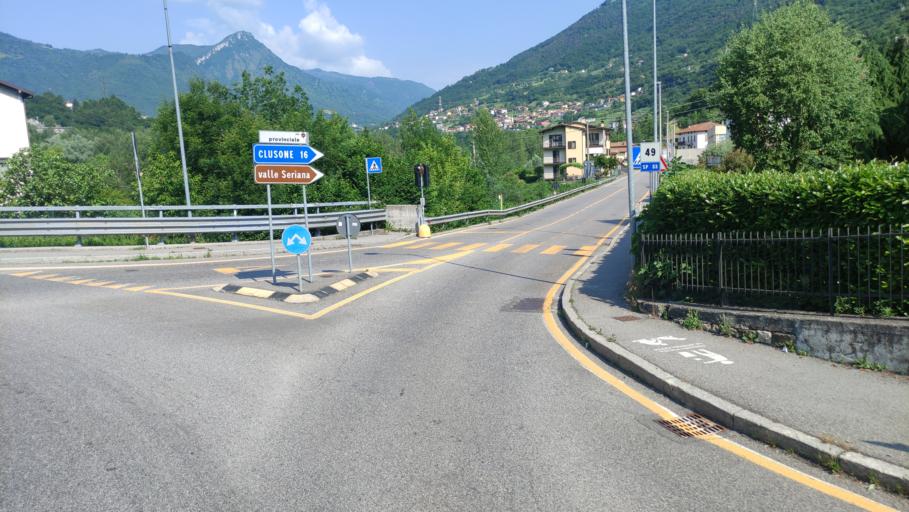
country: IT
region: Lombardy
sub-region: Provincia di Bergamo
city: Castro
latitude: 45.8073
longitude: 10.0609
